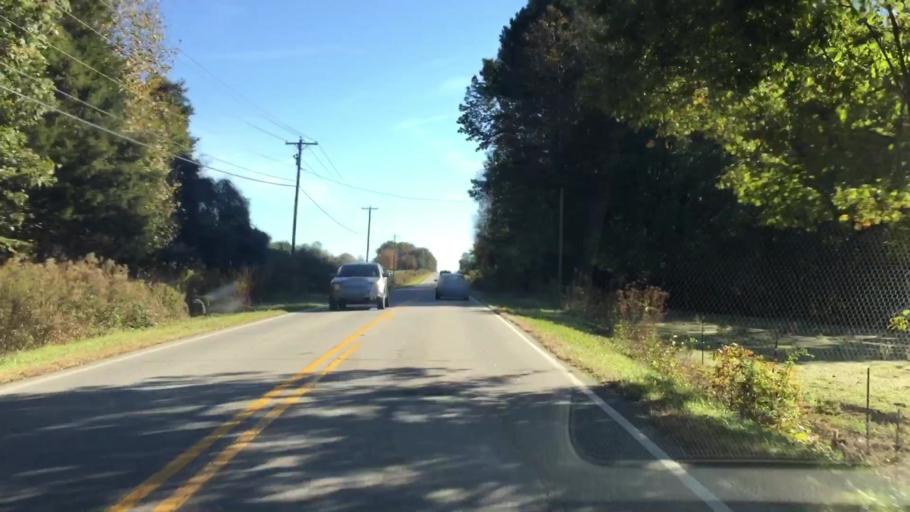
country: US
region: North Carolina
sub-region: Rowan County
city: China Grove
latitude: 35.6483
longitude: -80.6246
